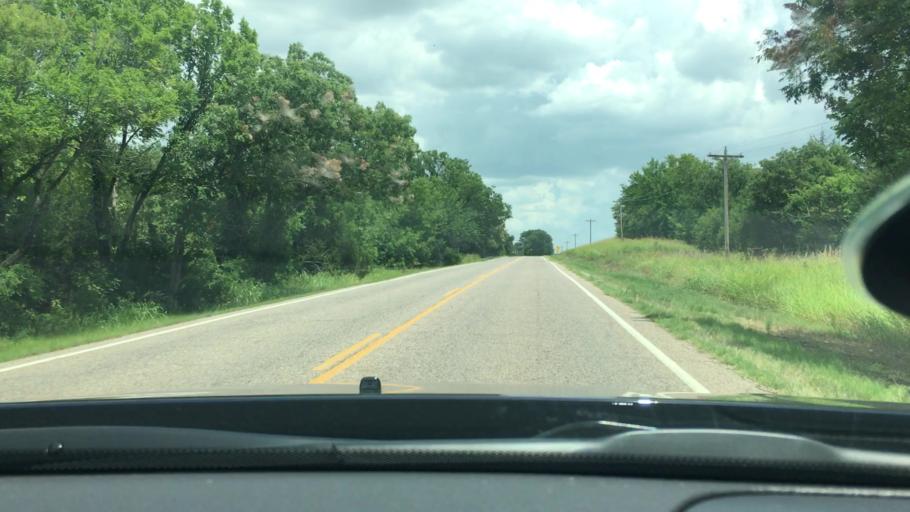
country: US
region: Texas
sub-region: Grayson County
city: Sherwood Shores
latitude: 33.9838
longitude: -96.8938
